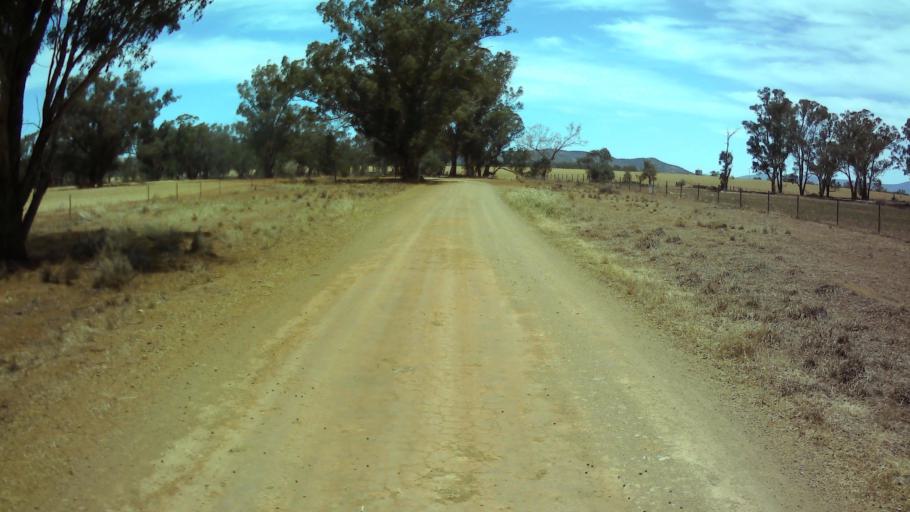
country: AU
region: New South Wales
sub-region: Weddin
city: Grenfell
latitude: -33.7569
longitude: 148.1433
